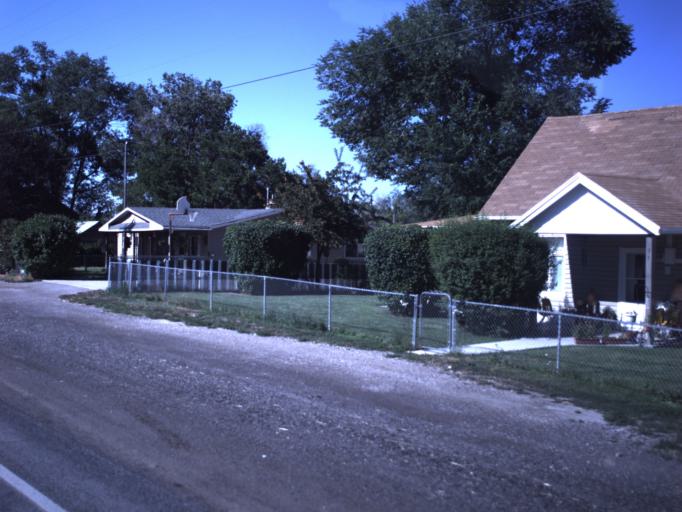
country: US
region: Utah
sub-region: Sanpete County
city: Manti
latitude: 39.1962
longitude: -111.6926
